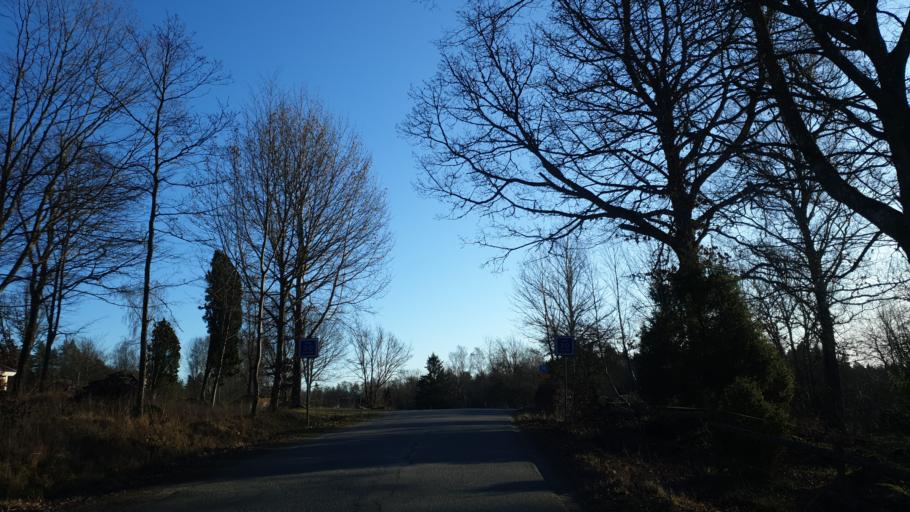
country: SE
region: Blekinge
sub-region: Ronneby Kommun
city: Brakne-Hoby
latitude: 56.2296
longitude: 15.1682
